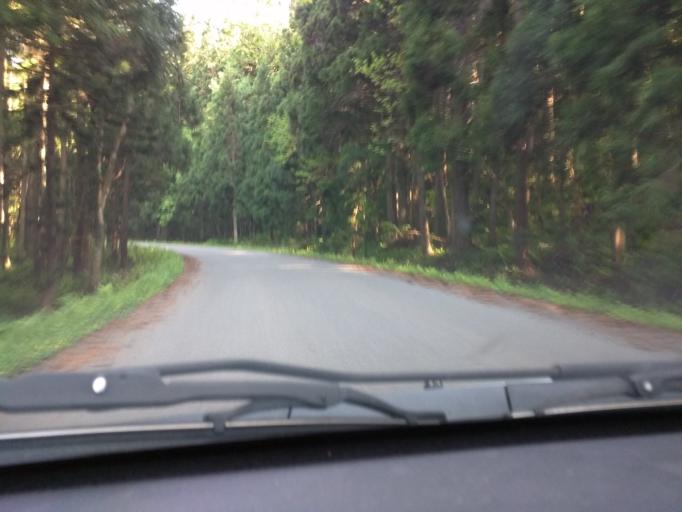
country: JP
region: Fukushima
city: Kitakata
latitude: 37.4859
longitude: 139.6642
